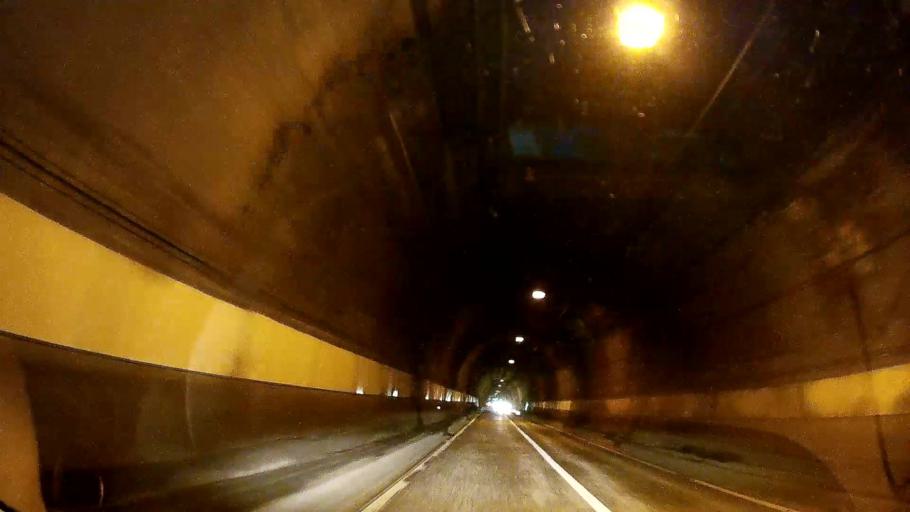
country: JP
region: Nagano
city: Toyoshina
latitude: 36.1543
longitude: 137.6809
